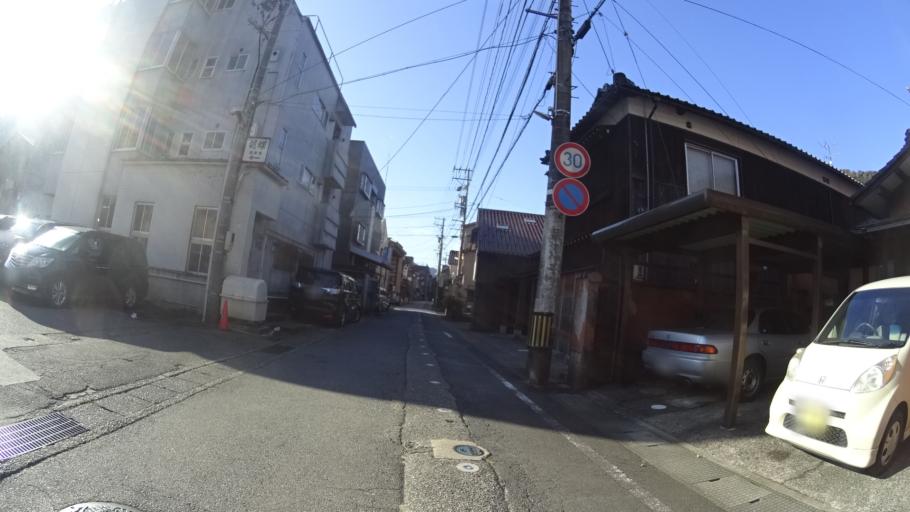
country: JP
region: Fukui
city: Maruoka
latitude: 36.2460
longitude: 136.3750
